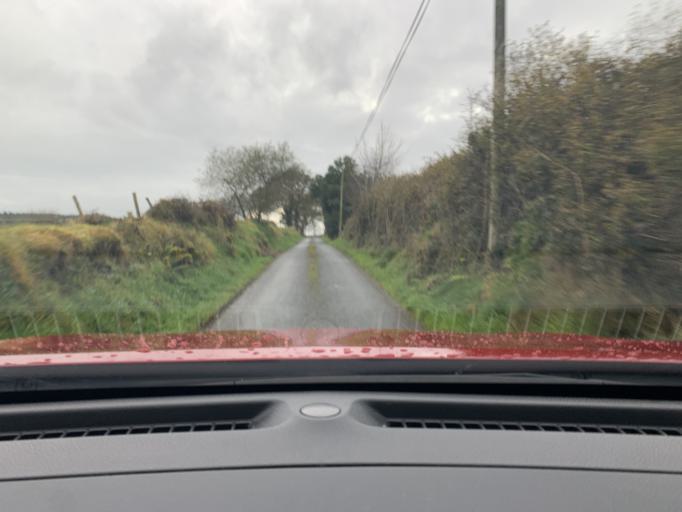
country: IE
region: Connaught
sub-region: Roscommon
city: Ballaghaderreen
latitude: 53.9670
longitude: -8.5729
